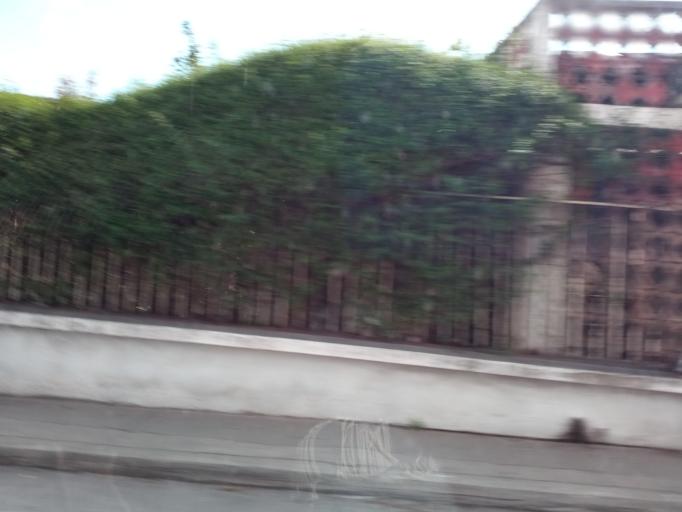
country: GT
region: Quetzaltenango
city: Quetzaltenango
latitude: 14.8547
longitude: -91.5382
